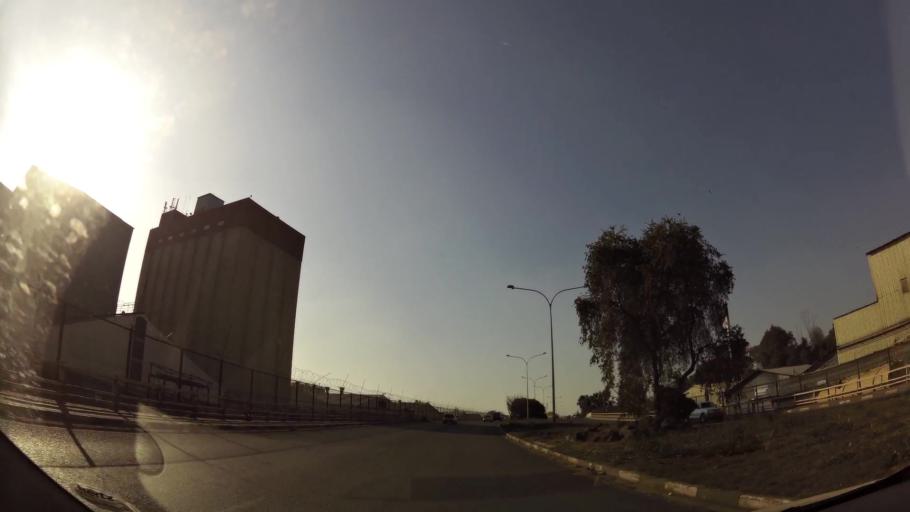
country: ZA
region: Gauteng
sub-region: West Rand District Municipality
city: Randfontein
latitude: -26.1621
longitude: 27.7136
